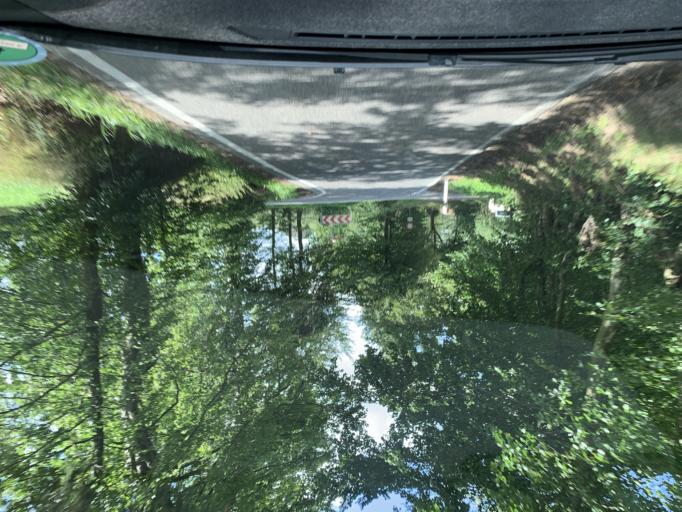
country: DE
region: North Rhine-Westphalia
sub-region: Regierungsbezirk Koln
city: Simmerath
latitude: 50.6028
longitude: 6.2677
